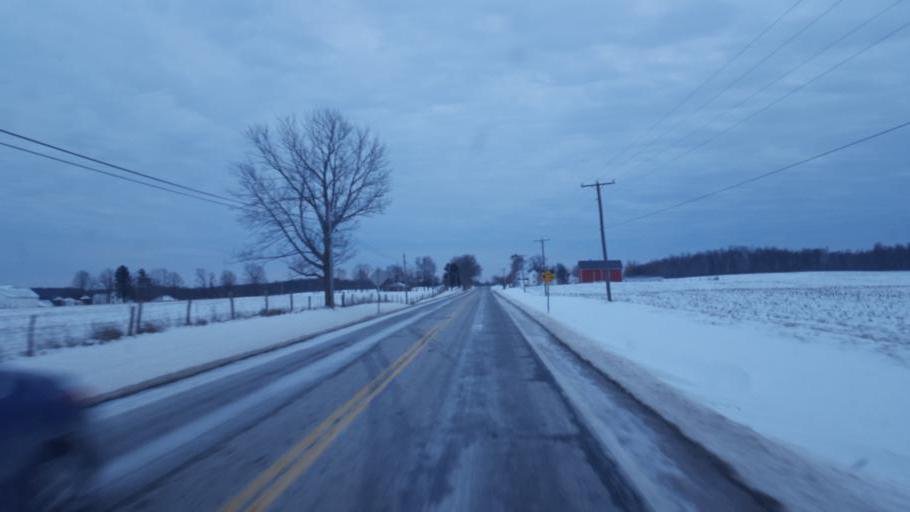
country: US
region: Ohio
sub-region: Richland County
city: Lexington
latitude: 40.6141
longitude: -82.6628
